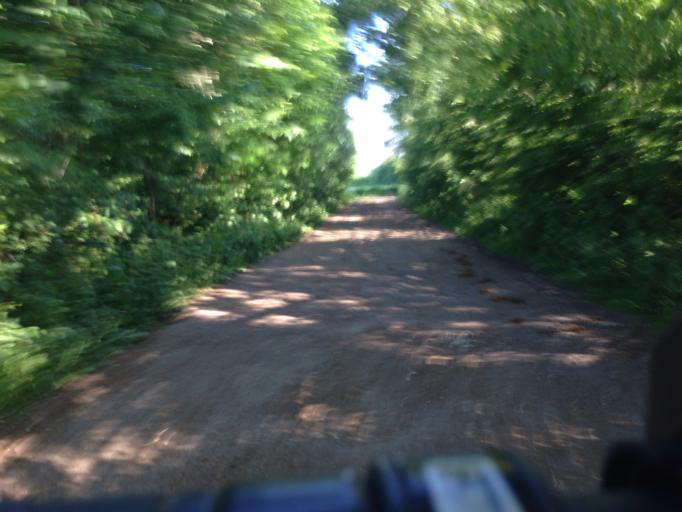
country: DE
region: Schleswig-Holstein
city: Stapelfeld
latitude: 53.5908
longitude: 10.1945
